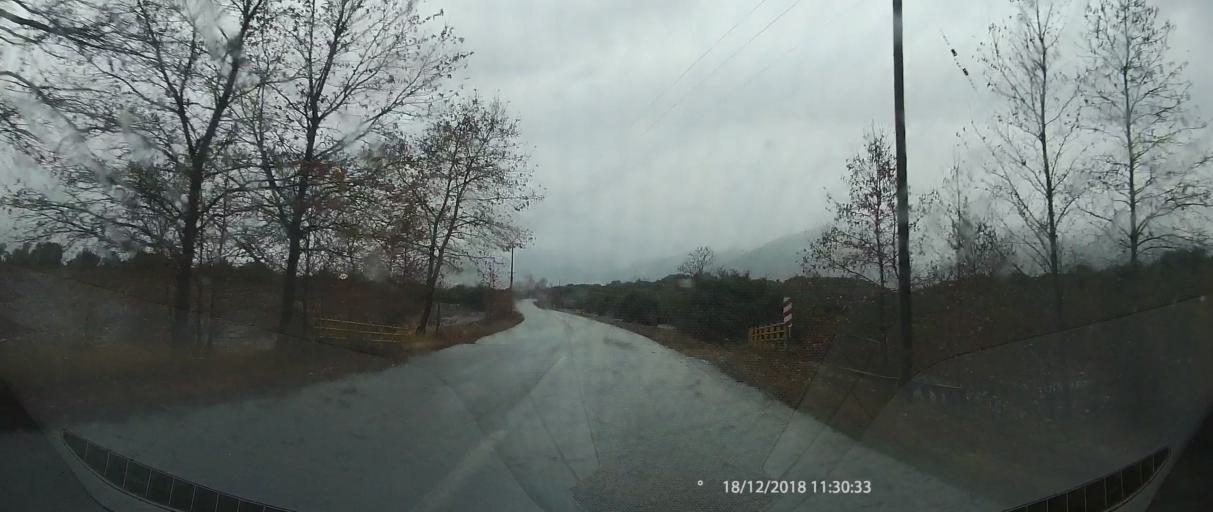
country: GR
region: Central Macedonia
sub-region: Nomos Pierias
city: Litochoro
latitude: 40.1214
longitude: 22.5203
